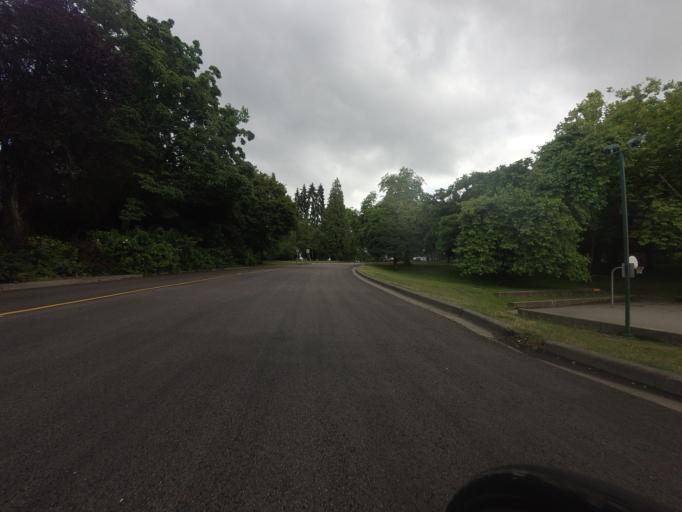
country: CA
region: British Columbia
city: West End
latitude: 49.2941
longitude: -123.1481
